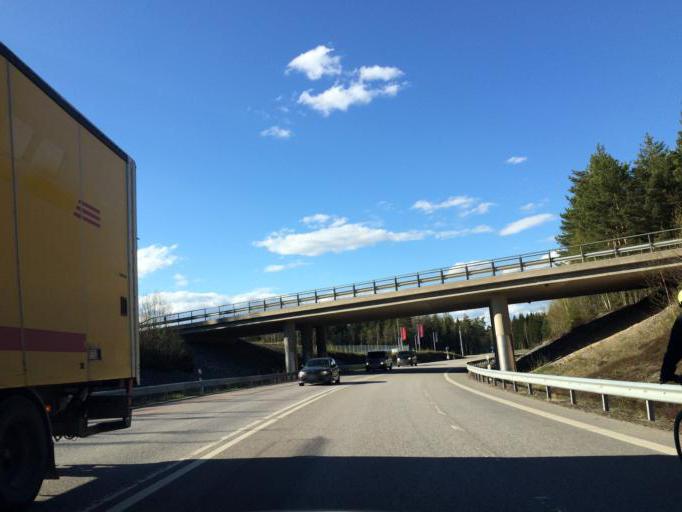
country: SE
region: Soedermanland
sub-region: Eskilstuna Kommun
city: Hallbybrunn
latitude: 59.4071
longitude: 16.3722
